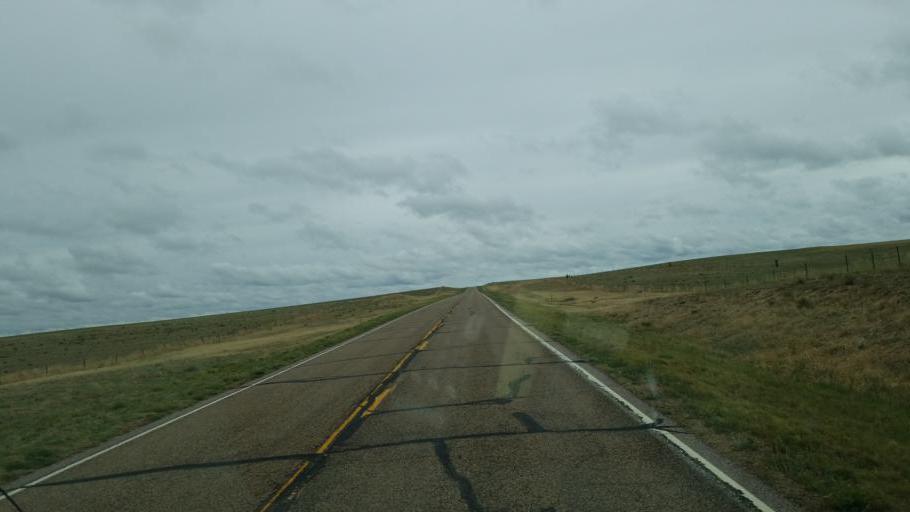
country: US
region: Colorado
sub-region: Lincoln County
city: Hugo
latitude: 38.8503
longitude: -103.4447
